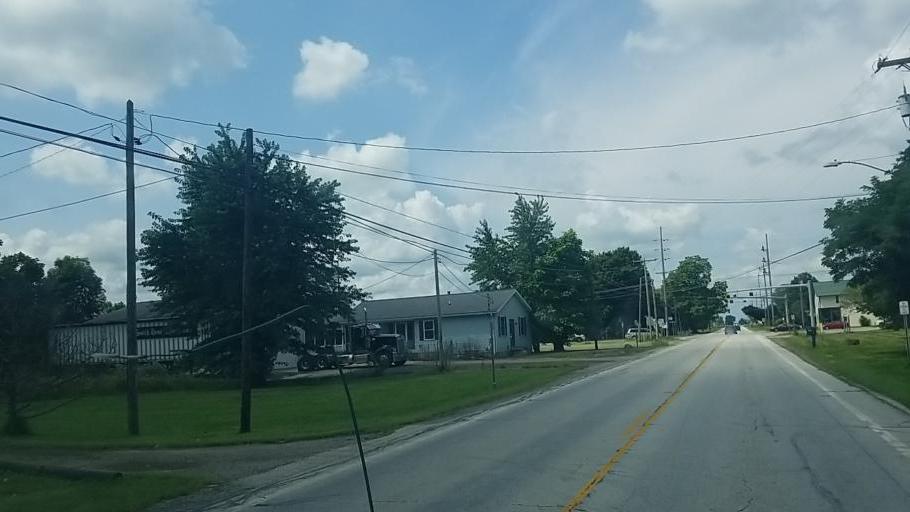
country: US
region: Ohio
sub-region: Wayne County
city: West Salem
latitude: 41.0272
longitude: -82.1246
